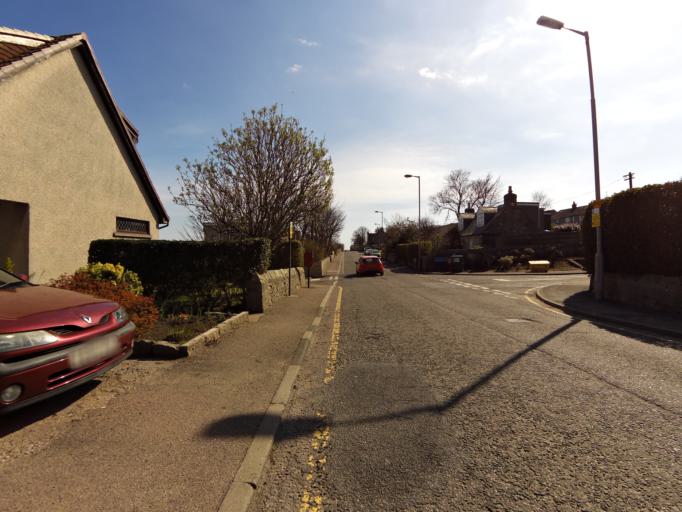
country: GB
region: Scotland
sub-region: Aberdeen City
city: Aberdeen
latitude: 57.1017
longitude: -2.0802
